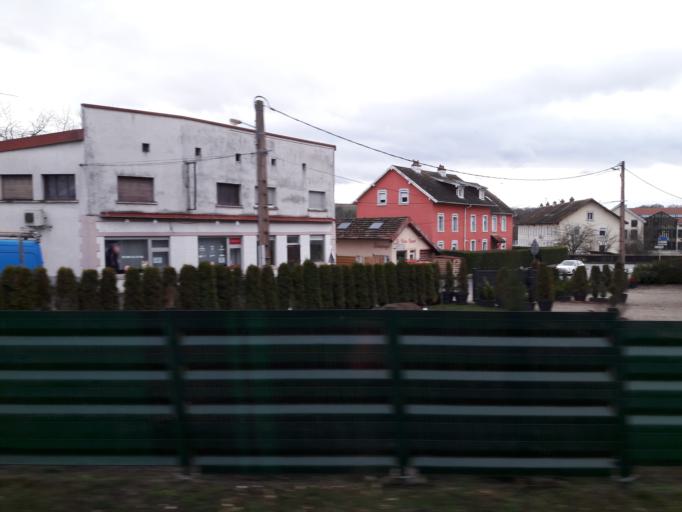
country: FR
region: Franche-Comte
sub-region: Territoire de Belfort
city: Grandvillars
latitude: 47.5372
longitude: 6.9812
